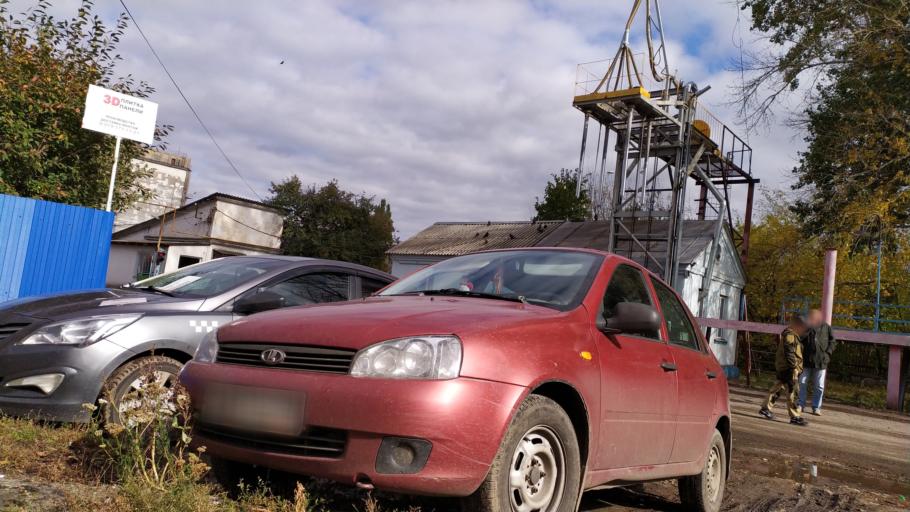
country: RU
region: Kursk
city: Kursk
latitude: 51.6509
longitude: 36.1469
